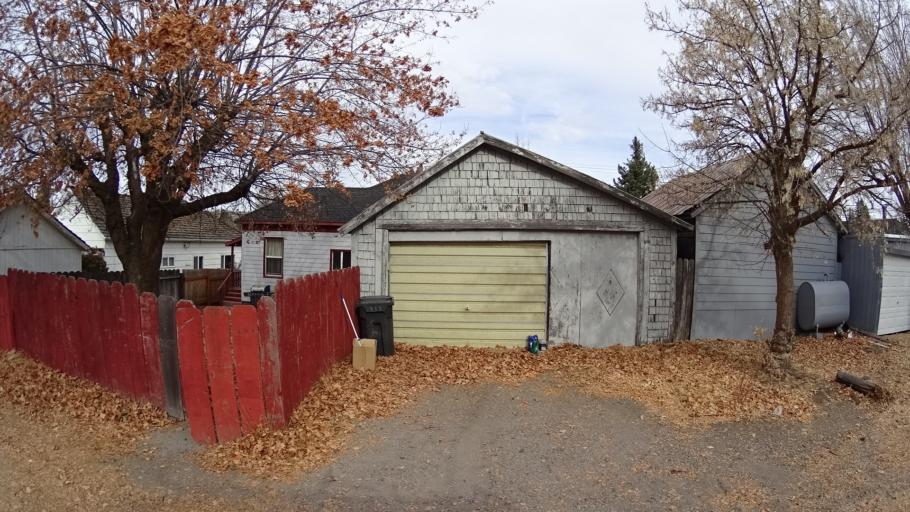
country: US
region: California
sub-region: Siskiyou County
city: Weed
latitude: 41.4250
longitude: -122.3853
